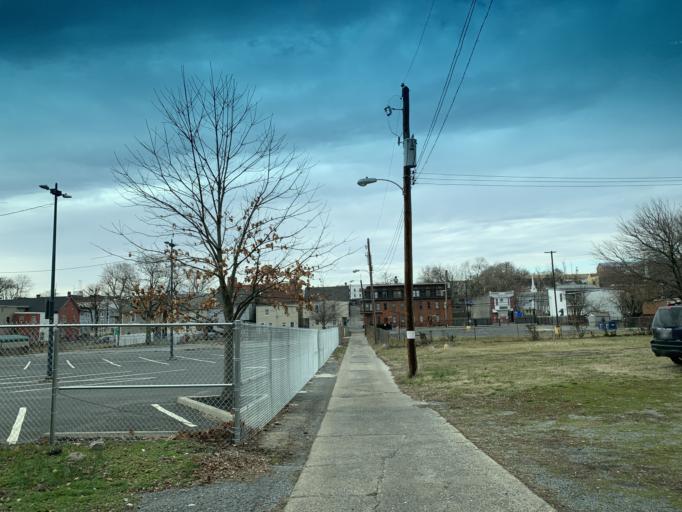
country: US
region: Maryland
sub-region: Washington County
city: Hagerstown
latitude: 39.6458
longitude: -77.7190
